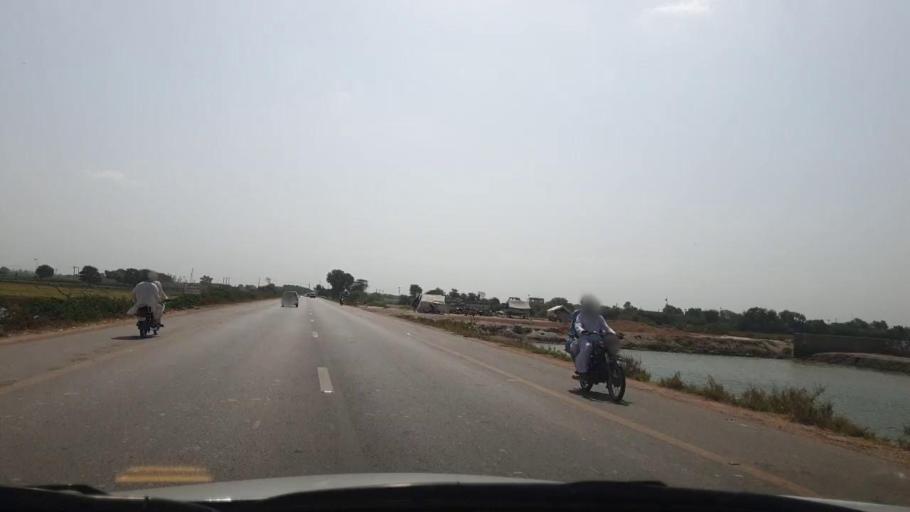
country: PK
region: Sindh
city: Matli
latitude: 25.0444
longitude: 68.6357
